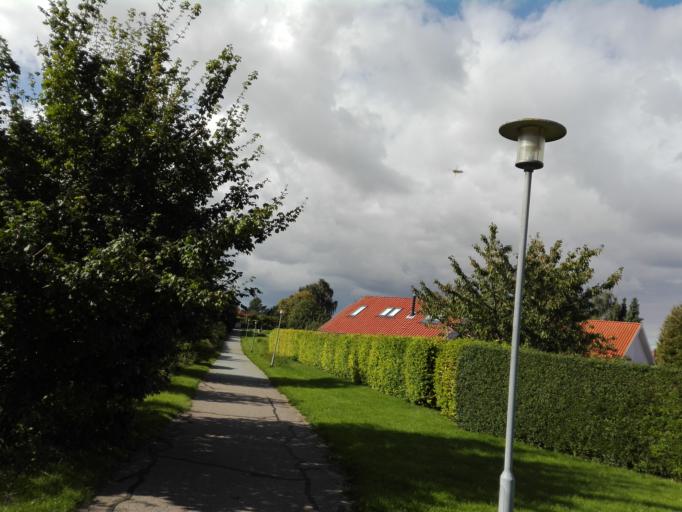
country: DK
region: Central Jutland
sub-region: Arhus Kommune
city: Beder
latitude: 56.0625
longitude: 10.2198
